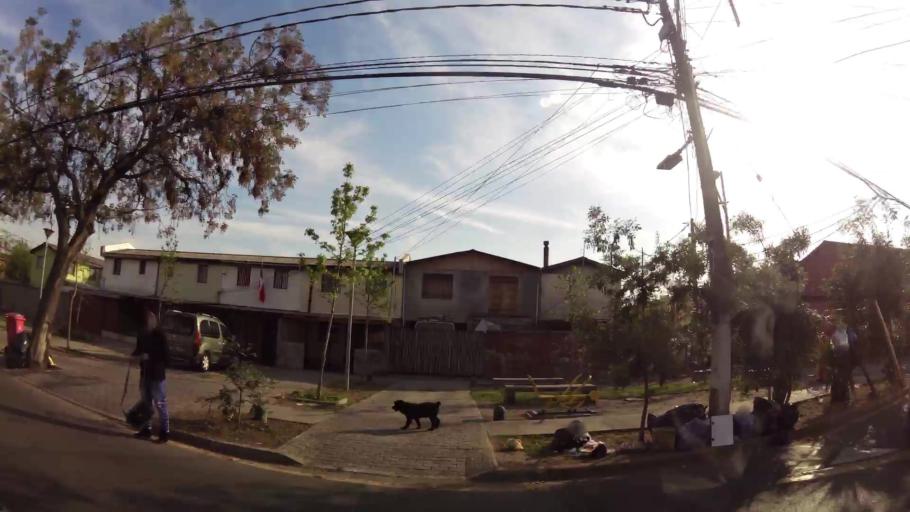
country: CL
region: Santiago Metropolitan
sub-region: Provincia de Santiago
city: Santiago
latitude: -33.5165
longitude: -70.6702
